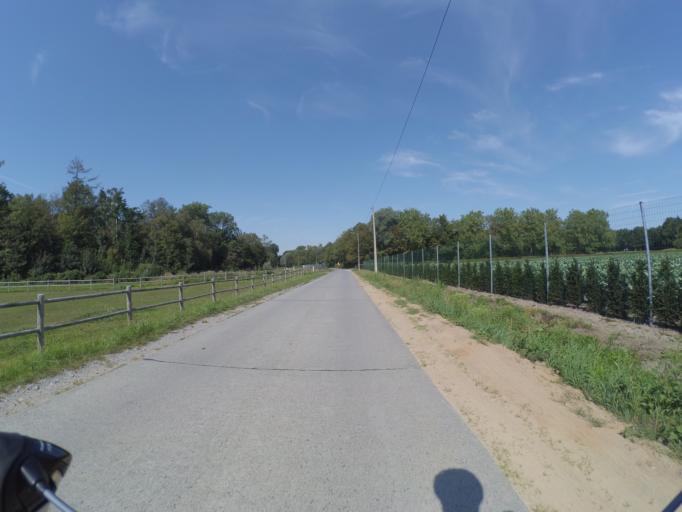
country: BE
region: Flanders
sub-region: Provincie West-Vlaanderen
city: Anzegem
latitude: 50.8739
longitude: 3.4655
